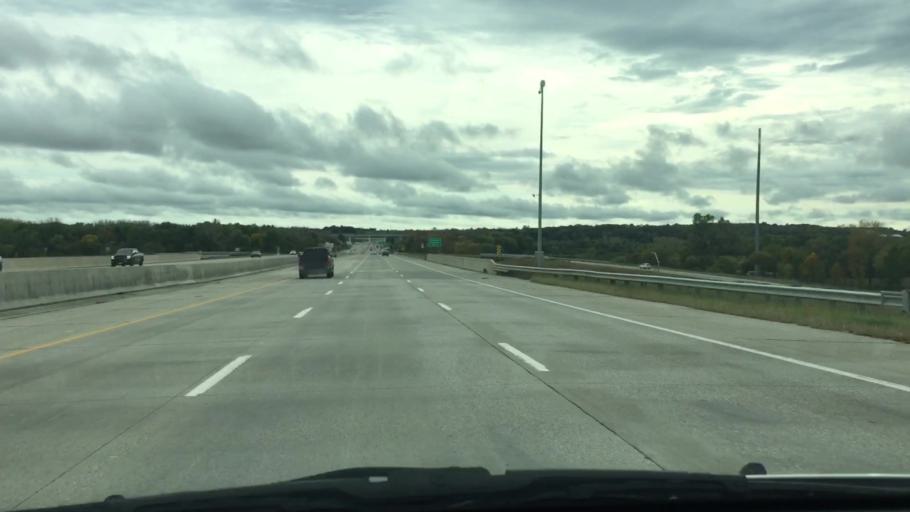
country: US
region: Iowa
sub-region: Polk County
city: West Des Moines
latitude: 41.5421
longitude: -93.7756
